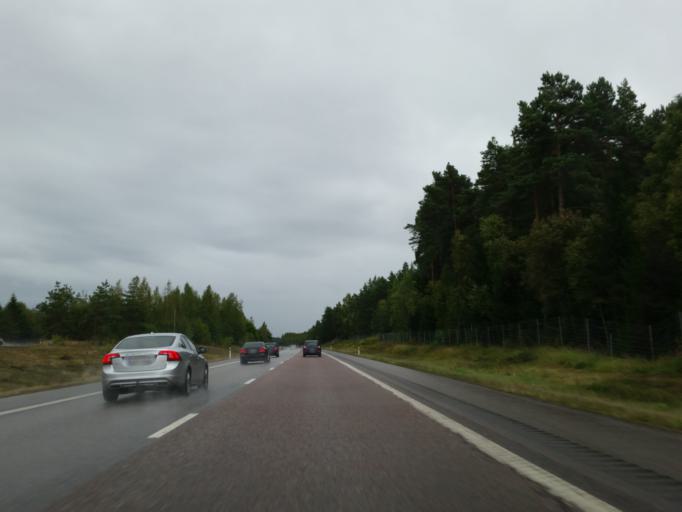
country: SE
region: Uppsala
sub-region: Enkopings Kommun
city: Dalby
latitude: 59.6131
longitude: 17.4082
